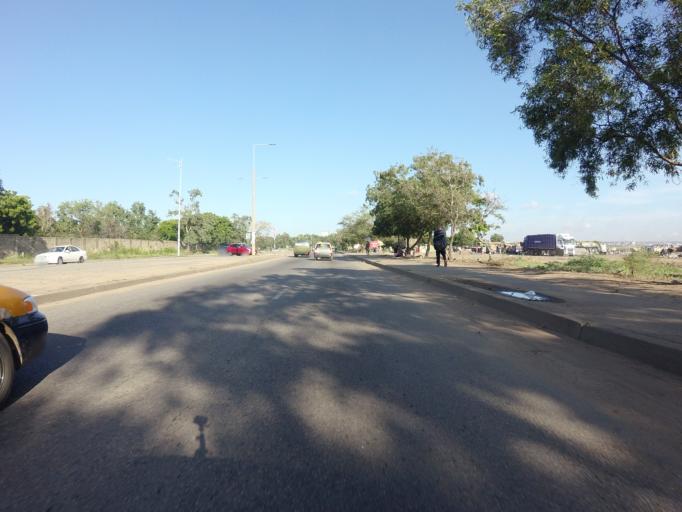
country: GH
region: Greater Accra
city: Accra
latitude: 5.5404
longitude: -0.2236
